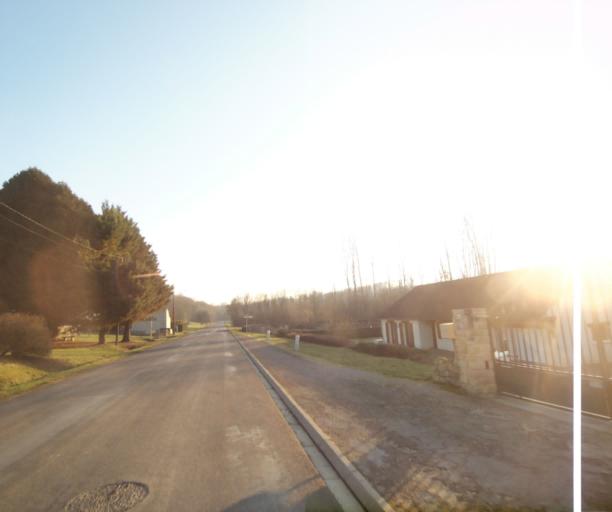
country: FR
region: Champagne-Ardenne
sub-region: Departement de la Haute-Marne
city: Chevillon
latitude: 48.5369
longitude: 5.1061
